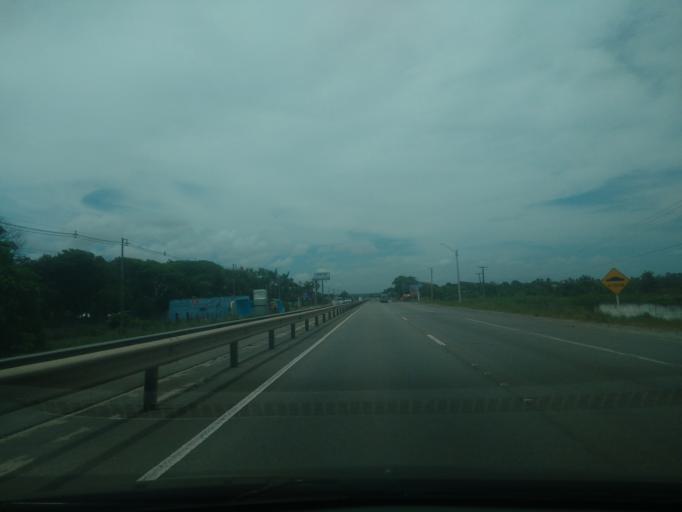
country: BR
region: Alagoas
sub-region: Marechal Deodoro
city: Marechal Deodoro
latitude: -9.7604
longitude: -35.8439
